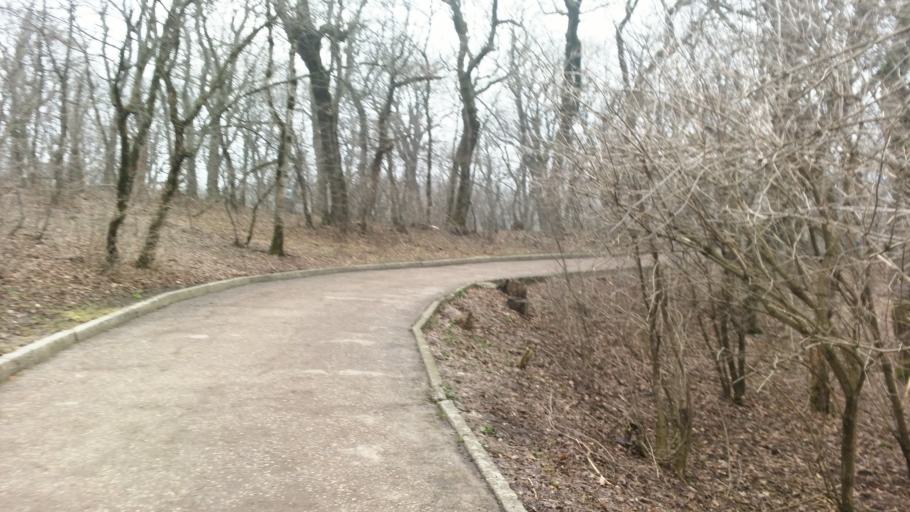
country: RU
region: Stavropol'skiy
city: Zheleznovodsk
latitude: 44.1425
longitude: 43.0347
